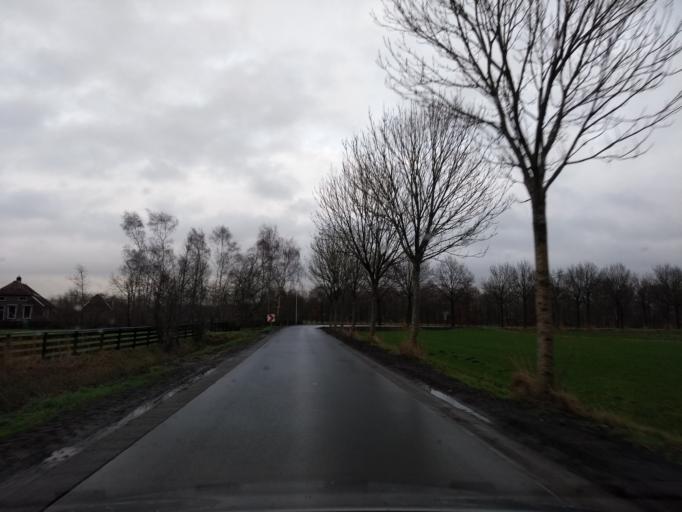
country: NL
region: Drenthe
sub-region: Gemeente De Wolden
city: Ruinen
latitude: 52.7269
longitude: 6.3234
